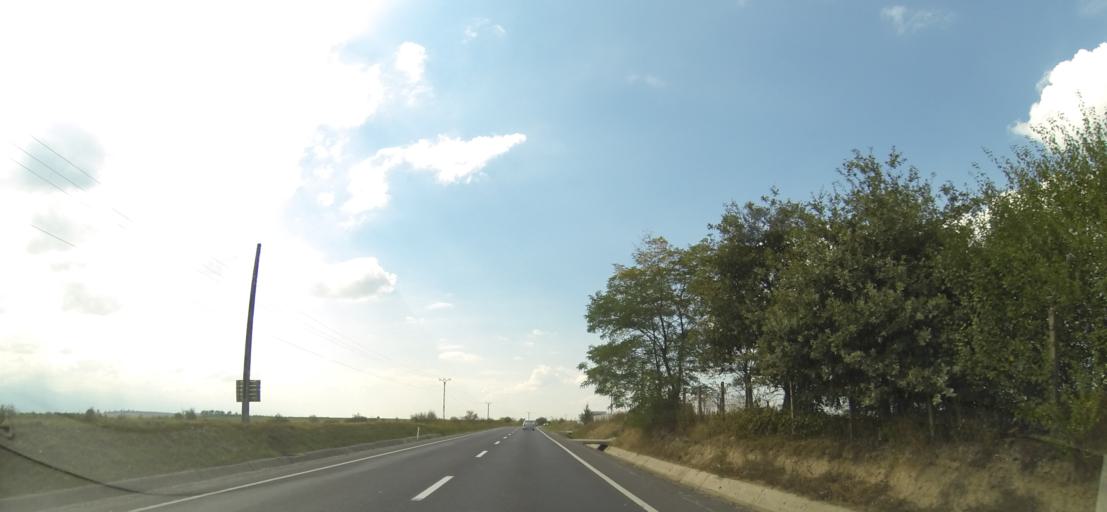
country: RO
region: Brasov
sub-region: Comuna Sercaia
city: Sercaia
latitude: 45.8304
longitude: 25.1329
